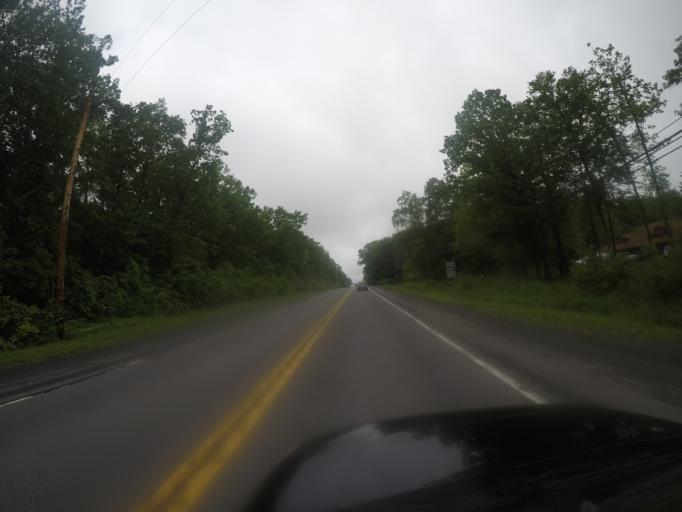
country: US
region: New York
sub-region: Ulster County
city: Shokan
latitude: 41.9795
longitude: -74.1864
